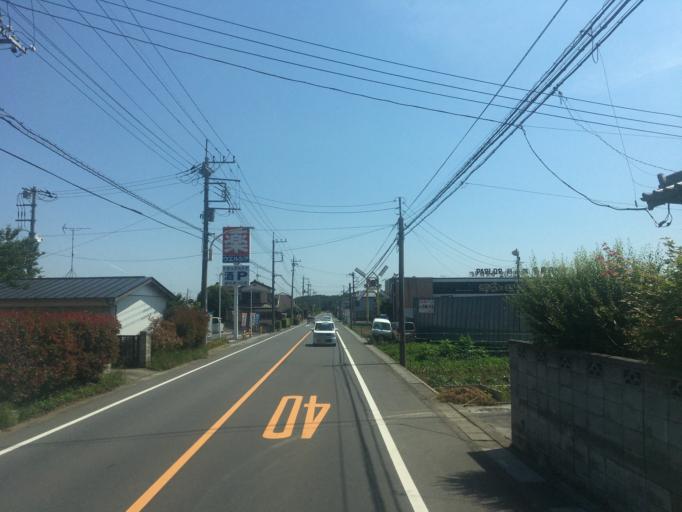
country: JP
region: Saitama
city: Ogawa
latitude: 36.0101
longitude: 139.3047
